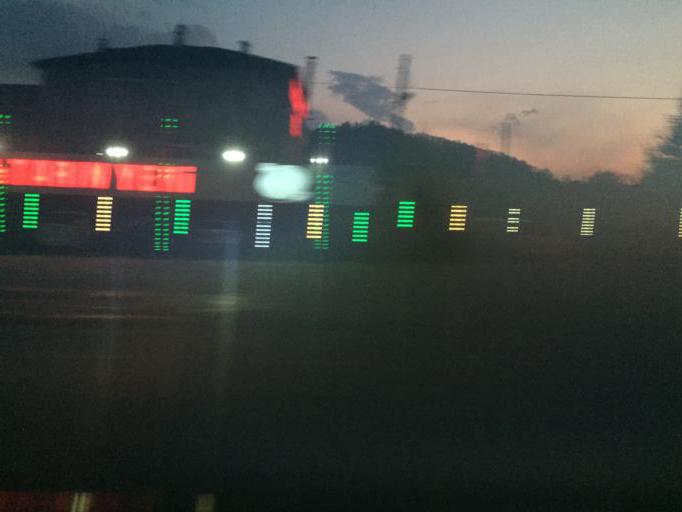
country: TR
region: Samsun
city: Kavak
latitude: 41.1381
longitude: 36.1238
